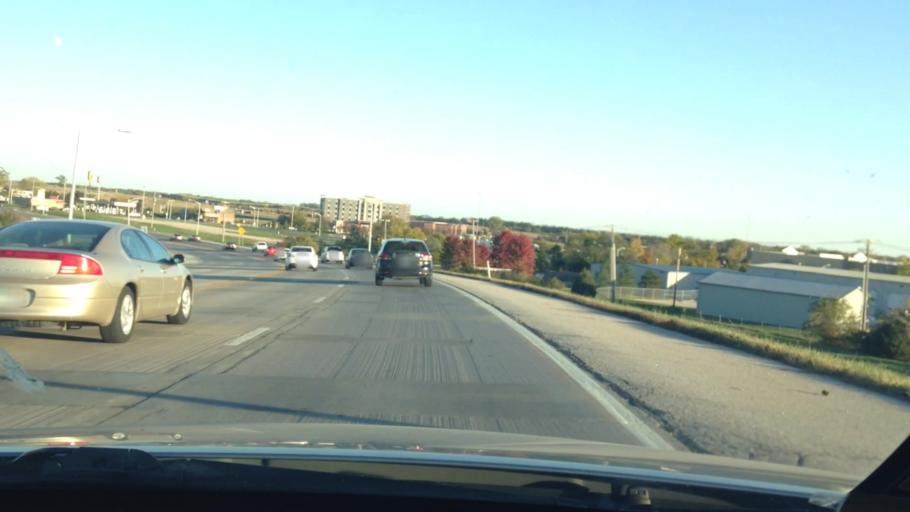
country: US
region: Kansas
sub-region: Johnson County
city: Gardner
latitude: 38.8129
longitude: -94.8950
